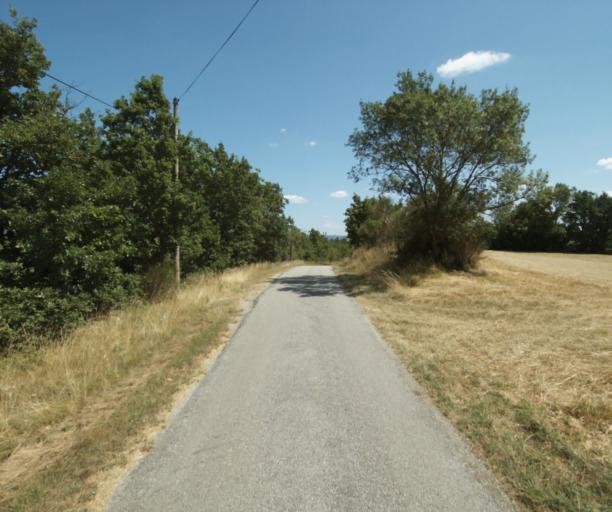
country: FR
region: Midi-Pyrenees
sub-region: Departement de la Haute-Garonne
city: Saint-Felix-Lauragais
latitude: 43.4736
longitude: 1.8819
